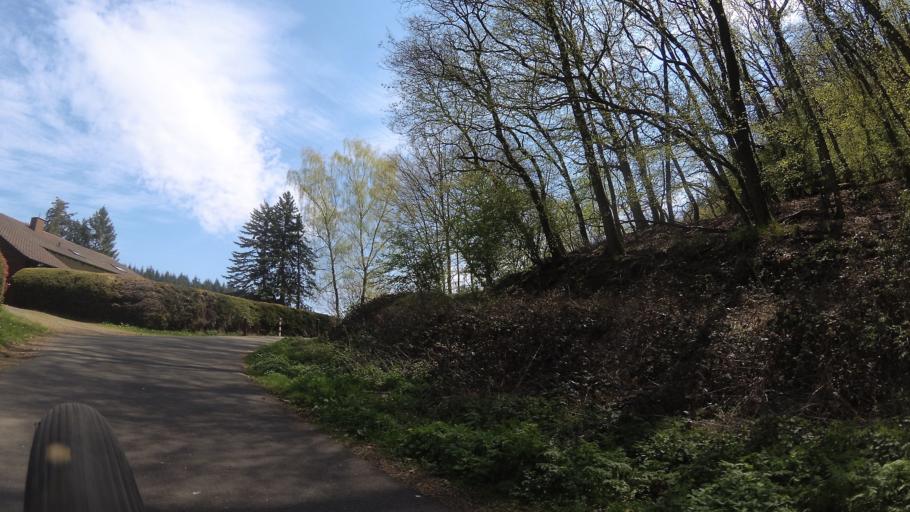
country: DE
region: Rheinland-Pfalz
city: Brucken
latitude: 49.4300
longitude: 7.3718
